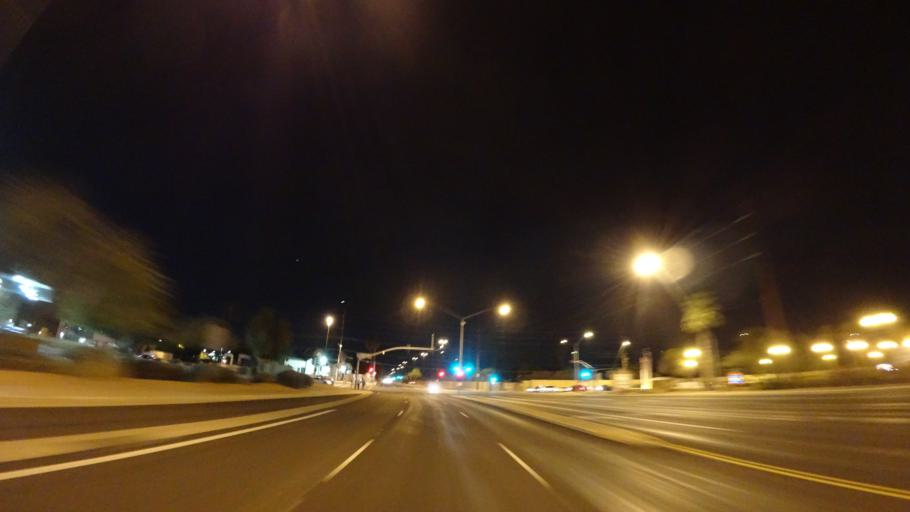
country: US
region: Arizona
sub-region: Maricopa County
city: Gilbert
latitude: 33.3939
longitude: -111.6840
